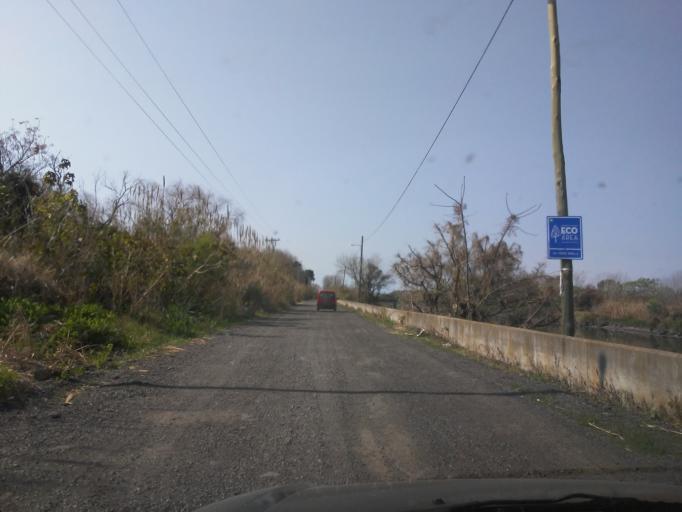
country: AR
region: Buenos Aires
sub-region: Partido de Avellaneda
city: Avellaneda
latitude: -34.6740
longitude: -58.3078
